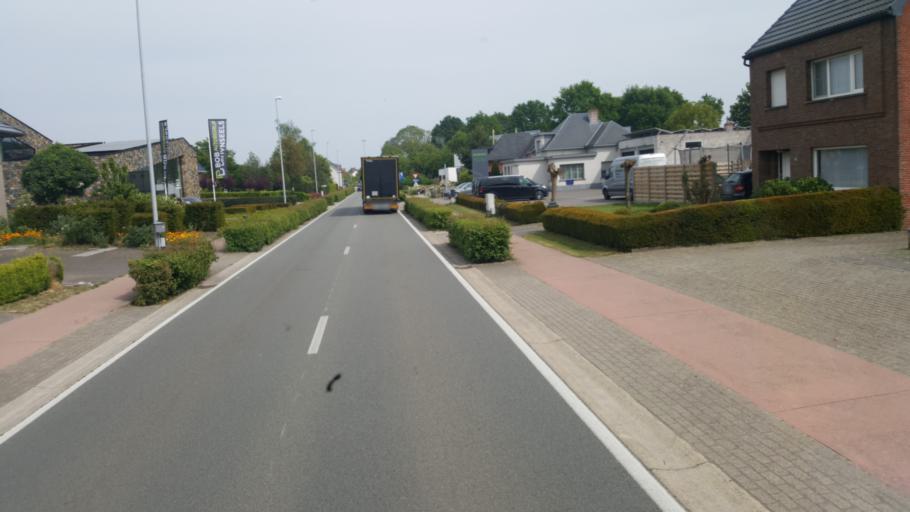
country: BE
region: Flanders
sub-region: Provincie Antwerpen
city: Herselt
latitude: 51.0882
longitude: 4.8658
